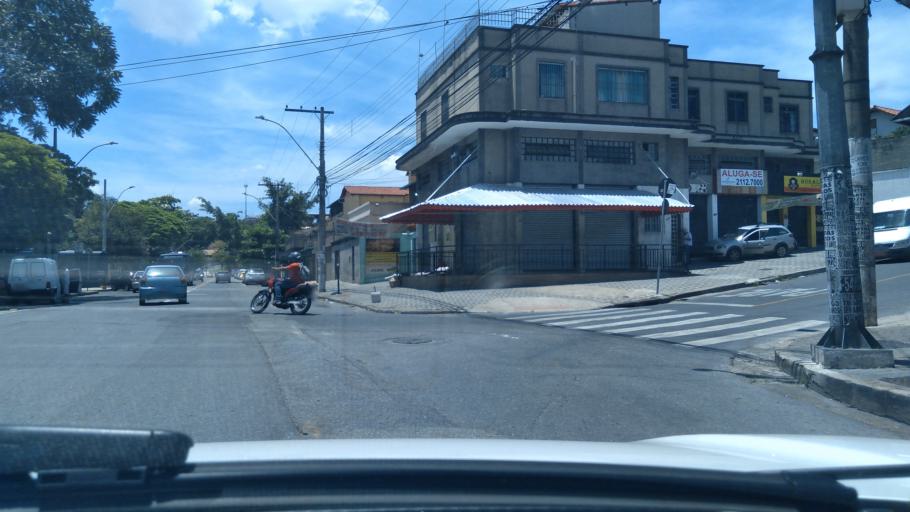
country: BR
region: Minas Gerais
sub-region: Contagem
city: Contagem
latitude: -19.9255
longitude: -43.9977
